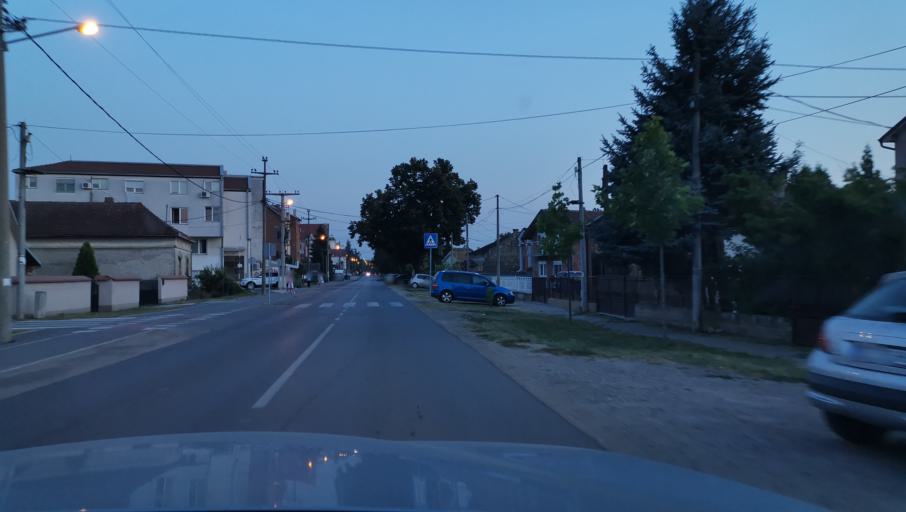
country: RS
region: Central Serbia
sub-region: Belgrade
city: Obrenovac
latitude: 44.6660
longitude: 20.2035
